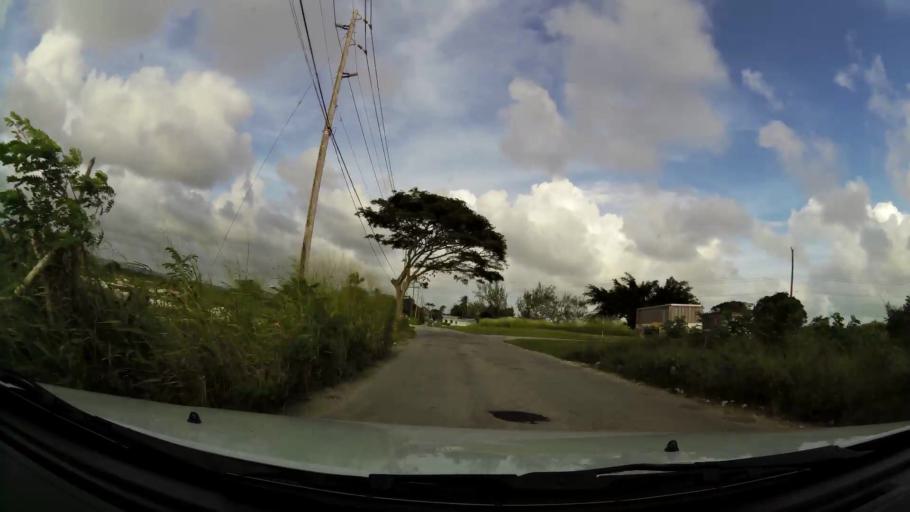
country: BB
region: Christ Church
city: Oistins
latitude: 13.0935
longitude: -59.5645
